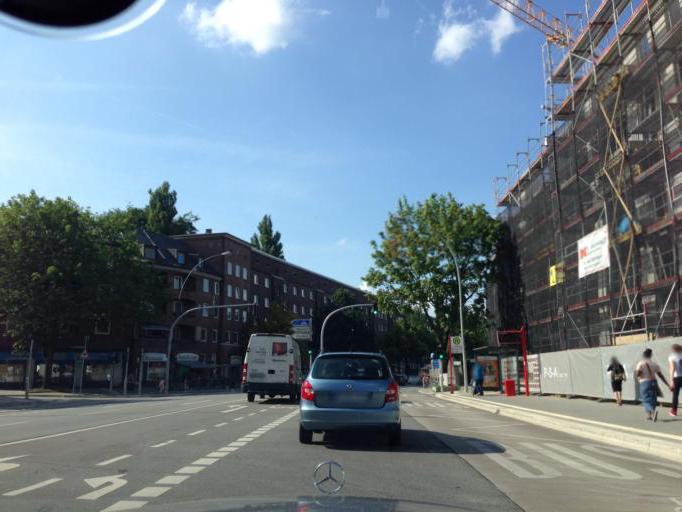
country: DE
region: Hamburg
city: Barmbek-Nord
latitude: 53.5989
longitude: 10.0417
